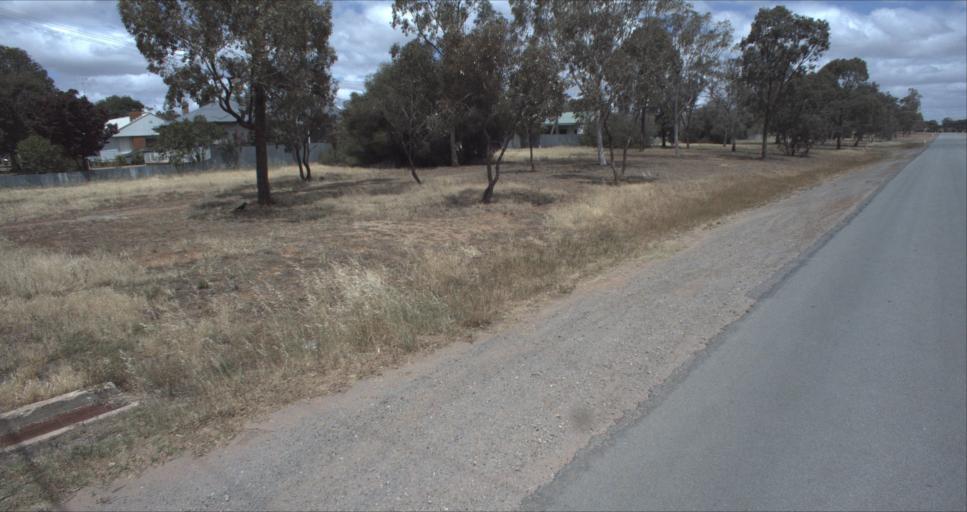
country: AU
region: New South Wales
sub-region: Leeton
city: Leeton
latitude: -34.5566
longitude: 146.3974
